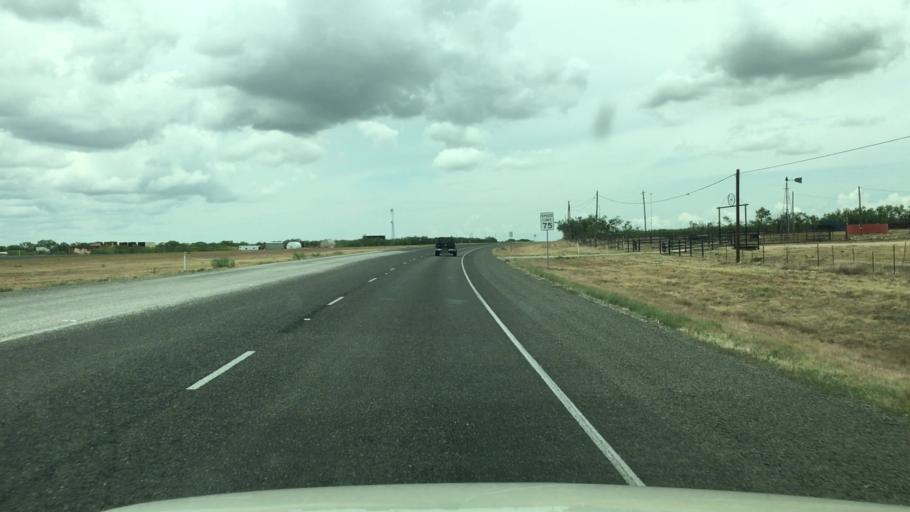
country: US
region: Texas
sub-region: Concho County
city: Eden
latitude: 31.2186
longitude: -99.9641
